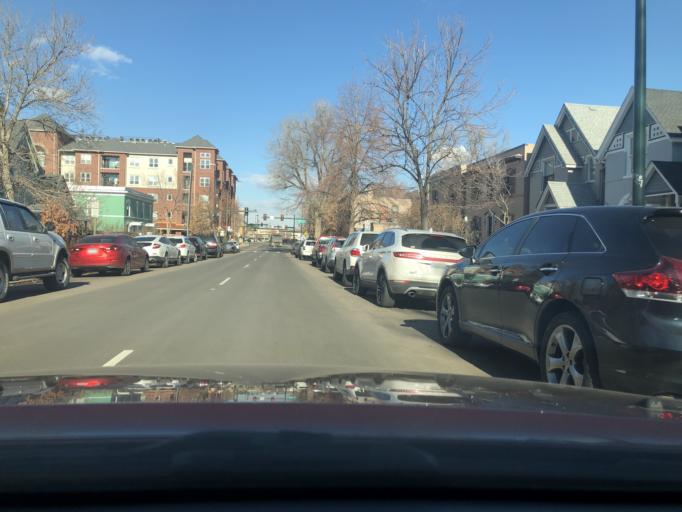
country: US
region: Colorado
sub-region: Denver County
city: Denver
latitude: 39.7453
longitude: -104.9775
